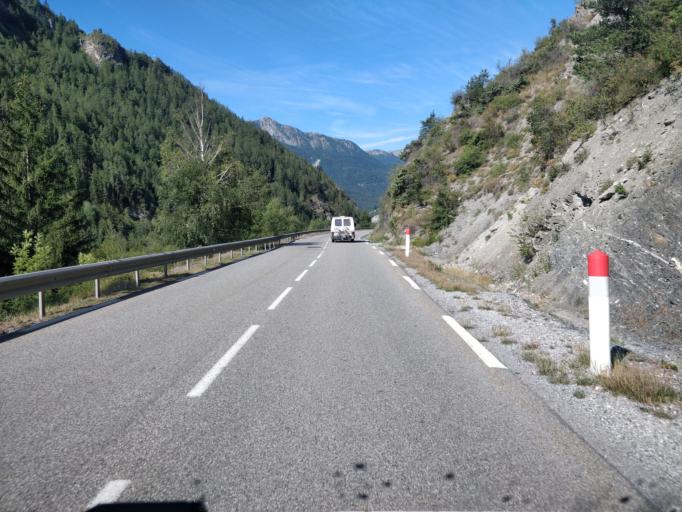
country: FR
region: Provence-Alpes-Cote d'Azur
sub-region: Departement des Alpes-de-Haute-Provence
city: Barcelonnette
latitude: 44.4006
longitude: 6.5225
